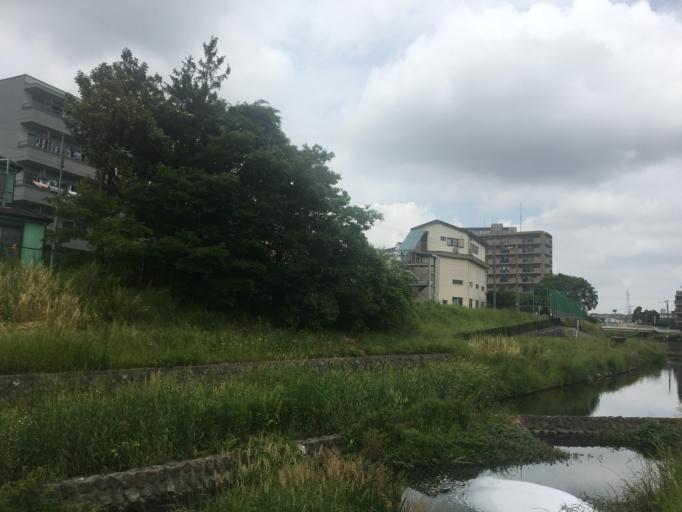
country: JP
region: Saitama
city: Kawaguchi
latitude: 35.8139
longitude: 139.7297
